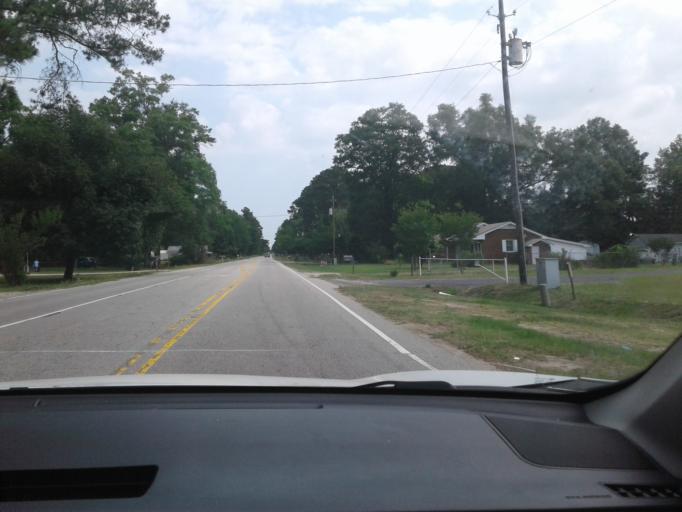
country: US
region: North Carolina
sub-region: Harnett County
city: Erwin
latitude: 35.3510
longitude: -78.6671
